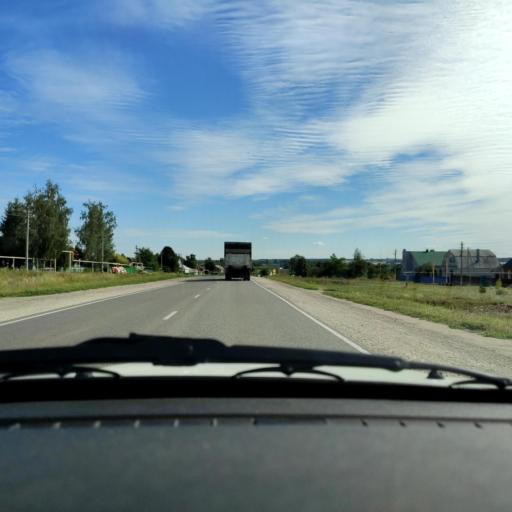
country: RU
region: Voronezj
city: Orlovo
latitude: 51.7462
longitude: 39.5807
